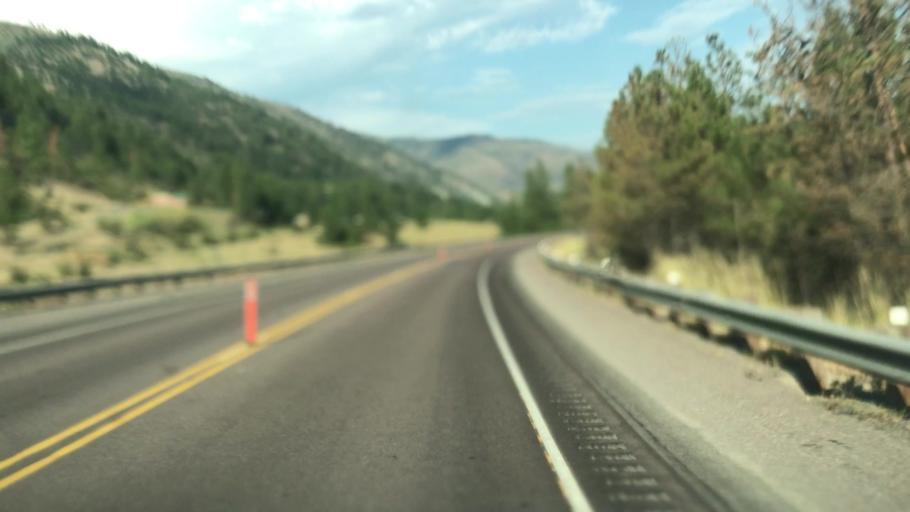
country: US
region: Montana
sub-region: Mineral County
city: Superior
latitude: 47.0184
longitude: -114.6795
